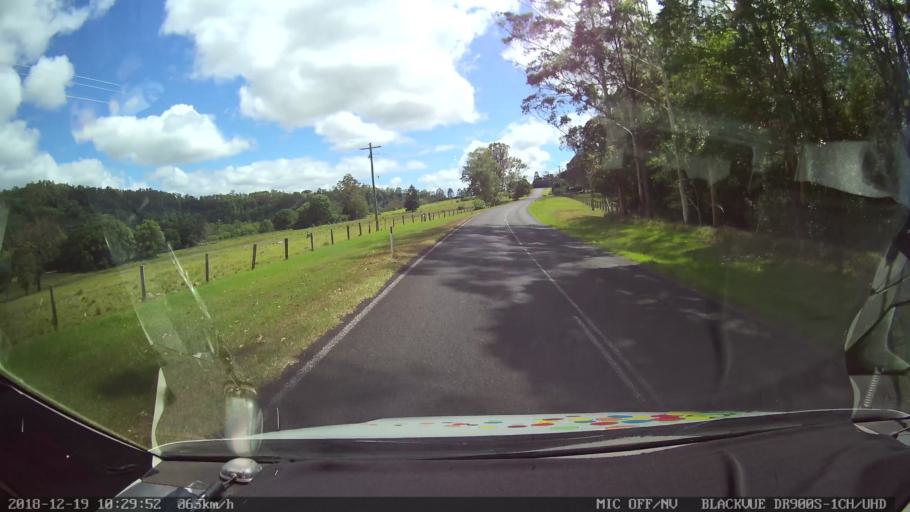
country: AU
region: New South Wales
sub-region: Lismore Municipality
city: Larnook
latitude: -28.5927
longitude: 153.1023
